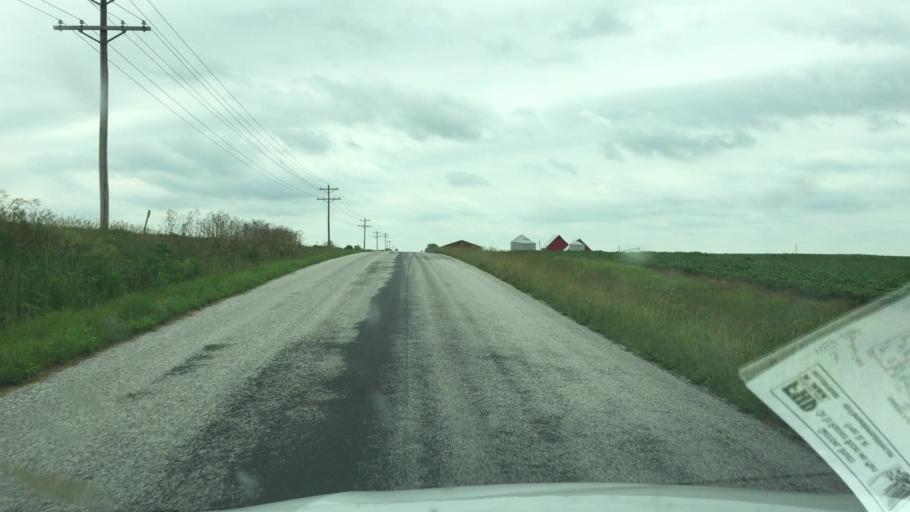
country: US
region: Illinois
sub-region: Hancock County
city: Carthage
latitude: 40.2937
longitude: -91.0833
